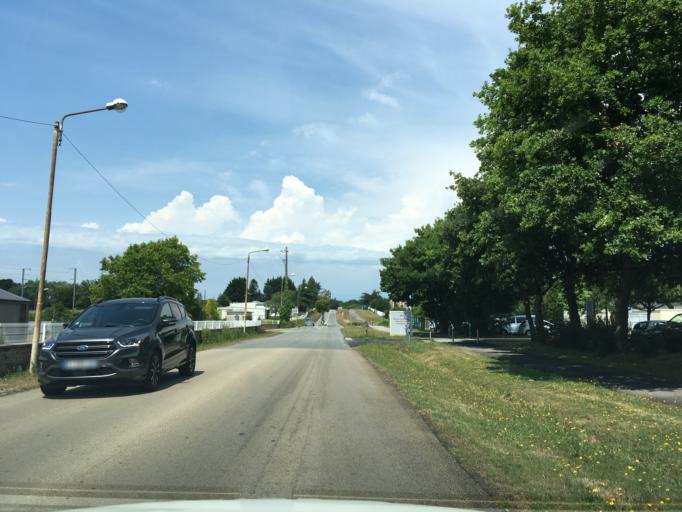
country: FR
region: Brittany
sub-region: Departement du Morbihan
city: Queven
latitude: 47.7726
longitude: -3.4047
